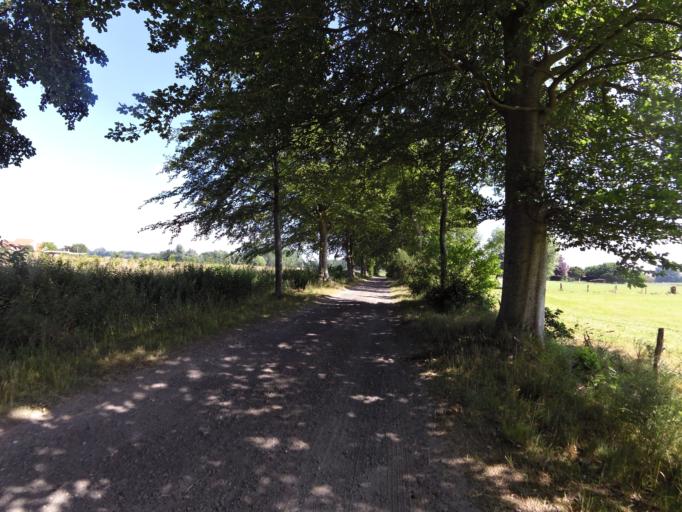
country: BE
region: Flanders
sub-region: Provincie West-Vlaanderen
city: Zedelgem
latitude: 51.1536
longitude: 3.1366
